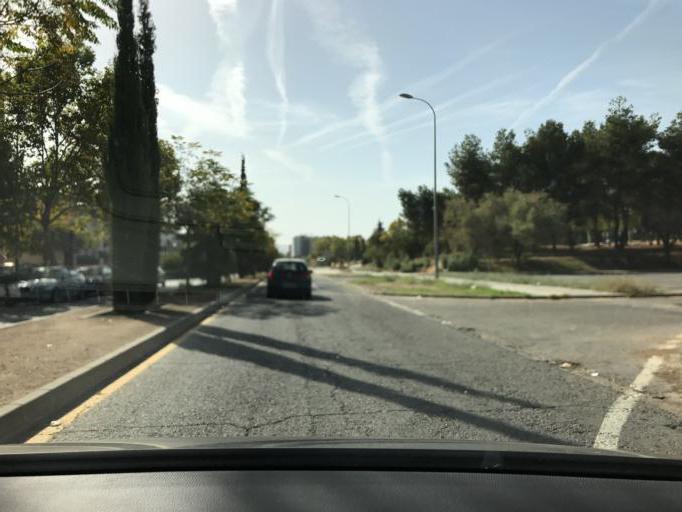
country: ES
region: Andalusia
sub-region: Provincia de Granada
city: Pulianas
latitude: 37.2055
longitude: -3.6127
